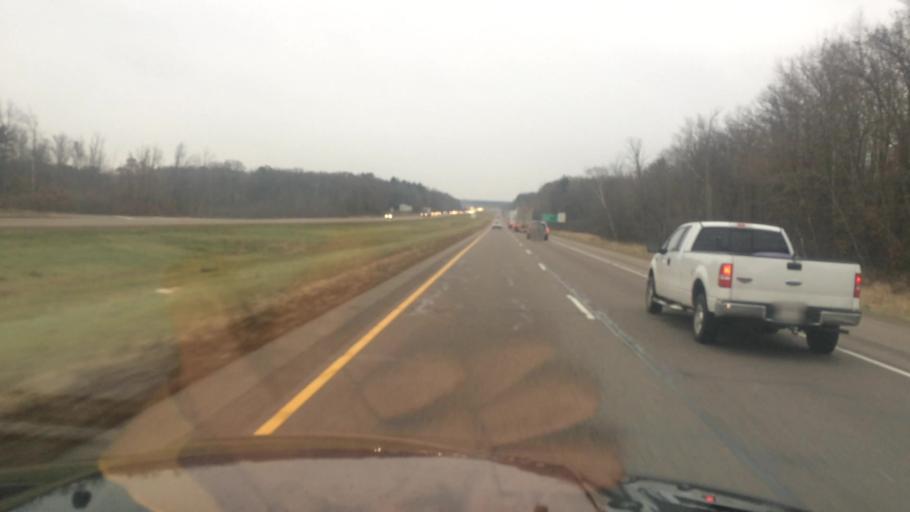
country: US
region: Wisconsin
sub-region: Portage County
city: Stevens Point
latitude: 44.5887
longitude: -89.6103
